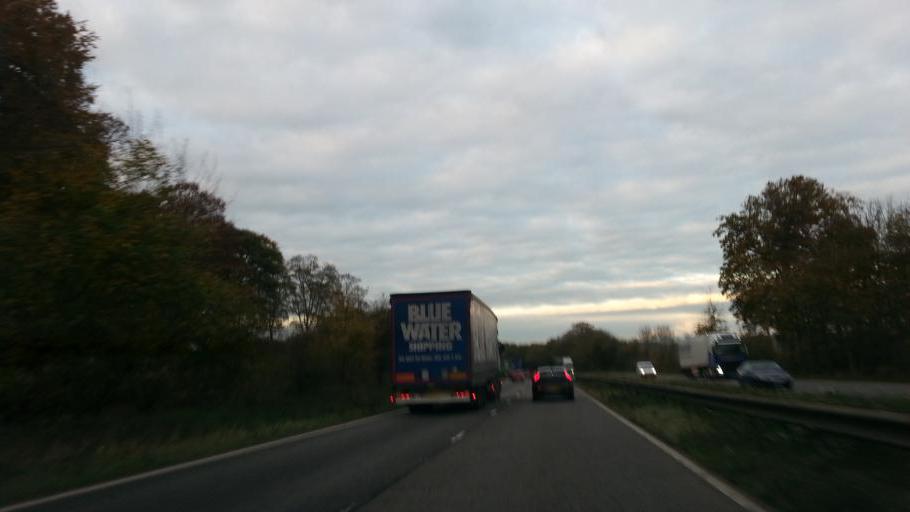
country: GB
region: England
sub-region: Lincolnshire
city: Grantham
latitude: 52.8489
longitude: -0.6275
